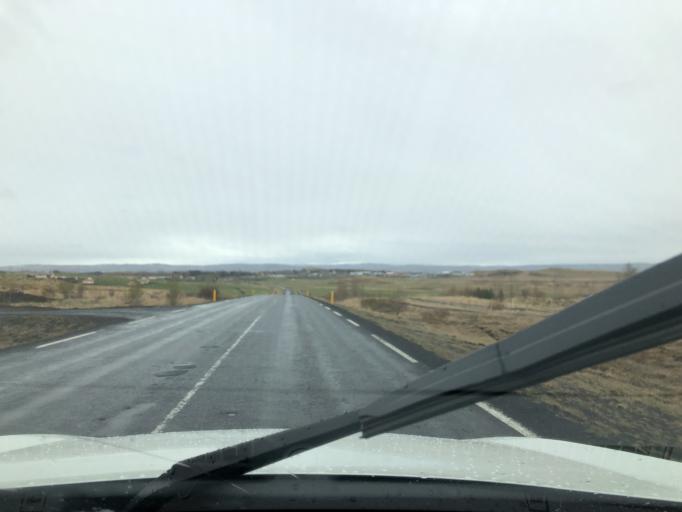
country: IS
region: South
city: Selfoss
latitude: 64.1763
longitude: -20.4816
